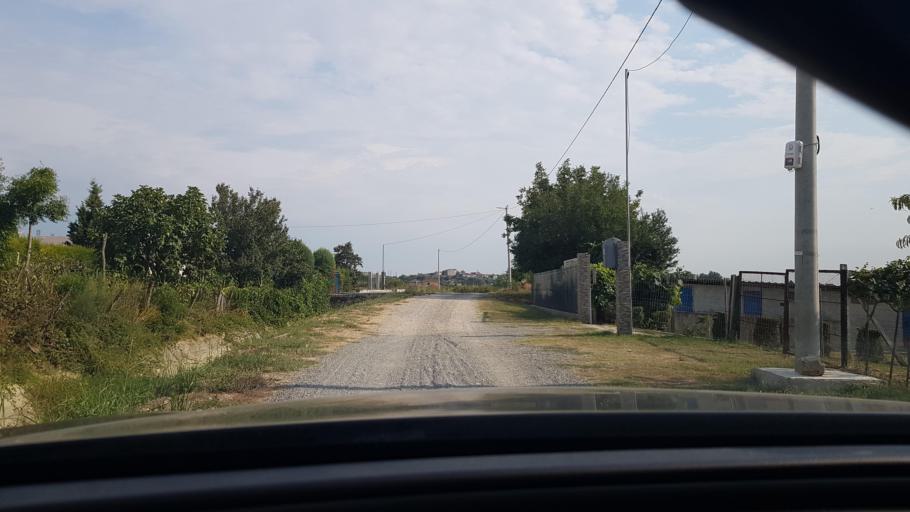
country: AL
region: Durres
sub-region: Rrethi i Durresit
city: Manze
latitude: 41.4724
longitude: 19.5669
